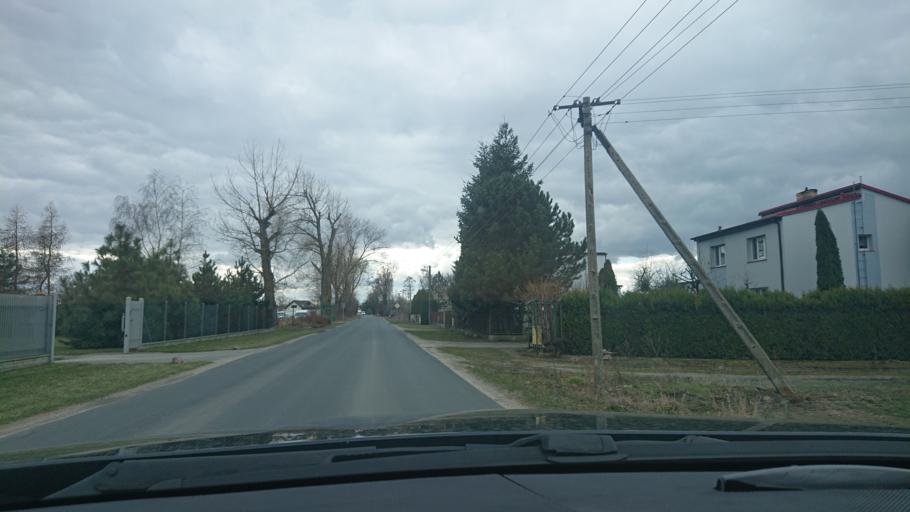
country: PL
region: Greater Poland Voivodeship
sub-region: Powiat gnieznienski
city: Gniezno
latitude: 52.5777
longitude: 17.6315
